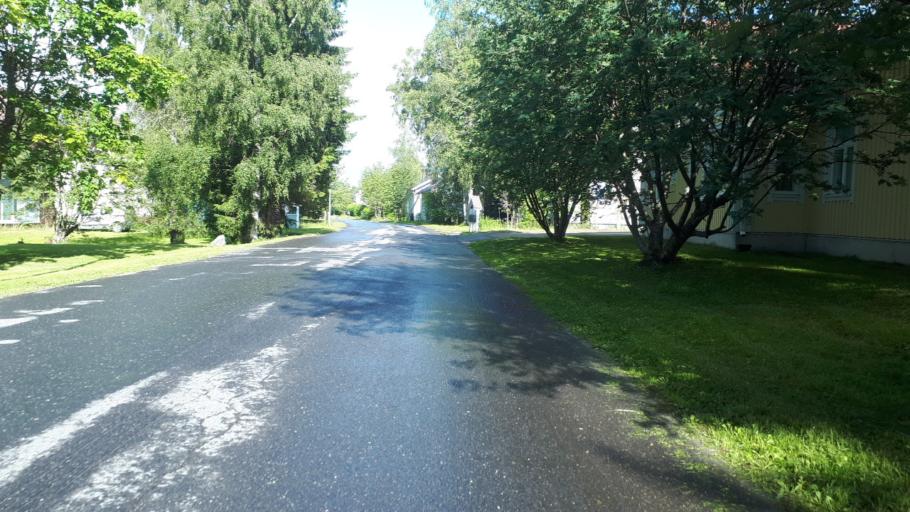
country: FI
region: Northern Ostrobothnia
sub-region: Oulunkaari
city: Ii
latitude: 65.3236
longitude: 25.3703
